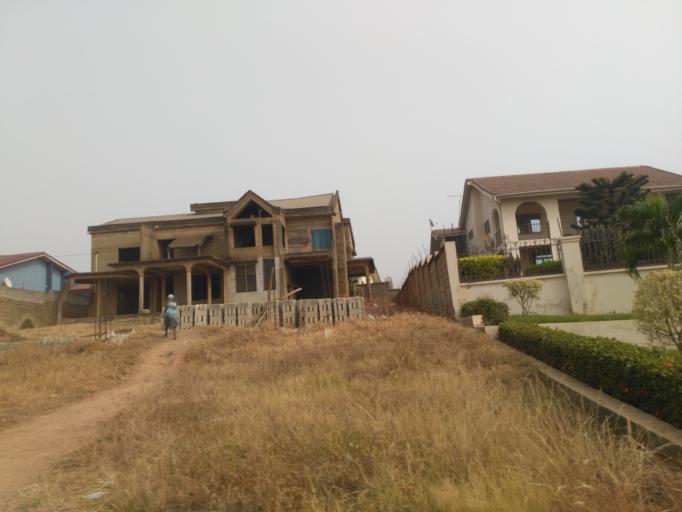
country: GH
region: Ashanti
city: Kumasi
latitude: 6.6408
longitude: -1.6286
